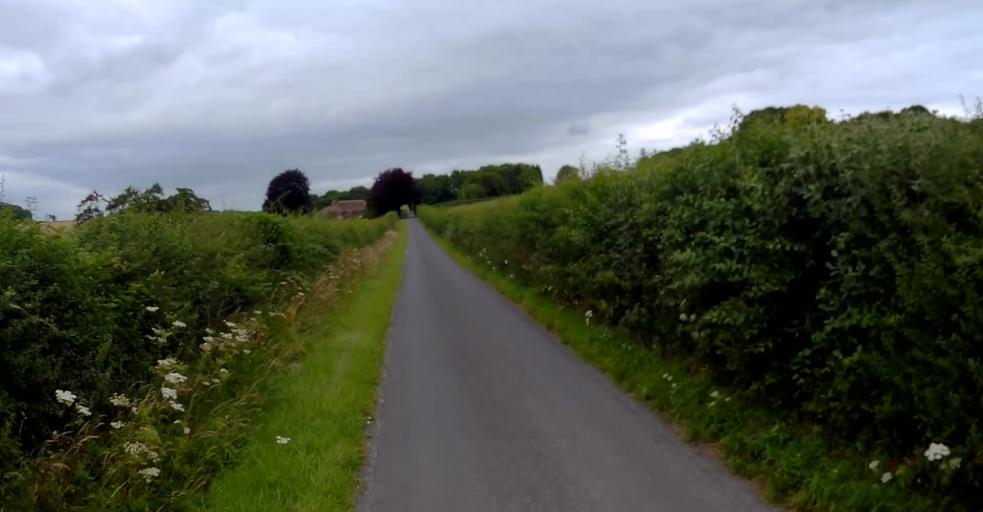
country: GB
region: England
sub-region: Hampshire
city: Kings Worthy
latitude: 51.0536
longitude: -1.2101
